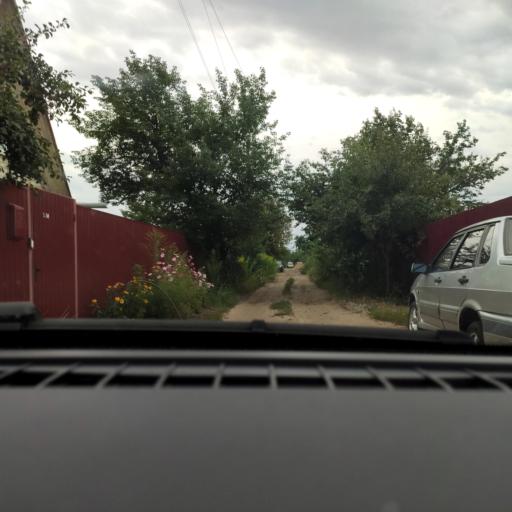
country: RU
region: Voronezj
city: Maslovka
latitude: 51.5215
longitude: 39.2350
